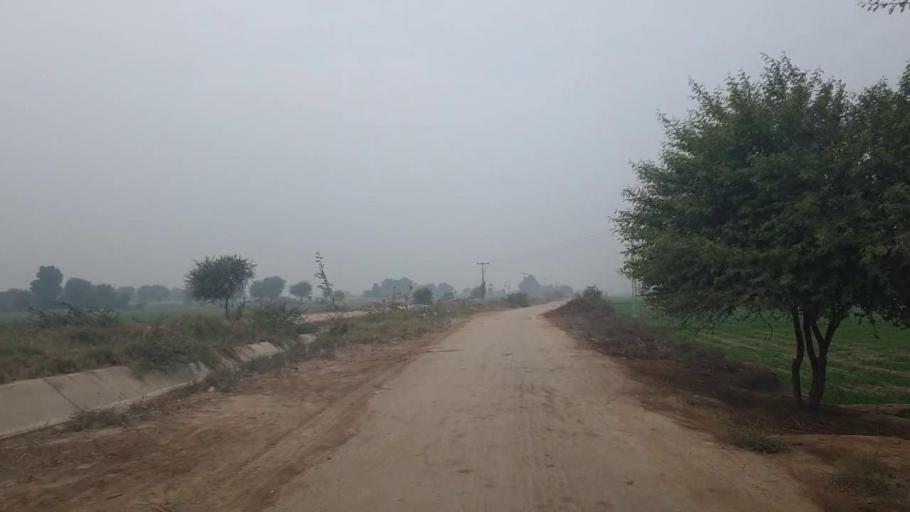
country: PK
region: Sindh
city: Tando Adam
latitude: 25.6898
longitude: 68.6708
